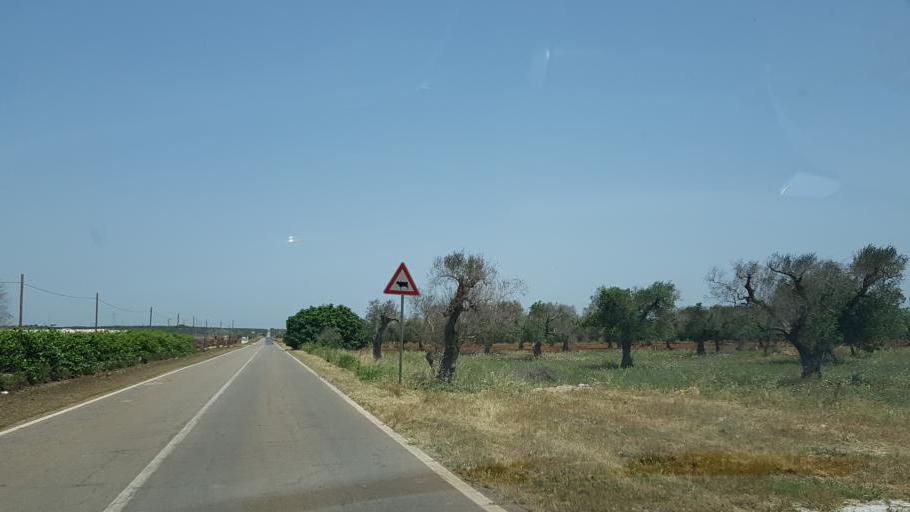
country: IT
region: Apulia
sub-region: Provincia di Lecce
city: Porto Cesareo
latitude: 40.2772
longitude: 17.9039
